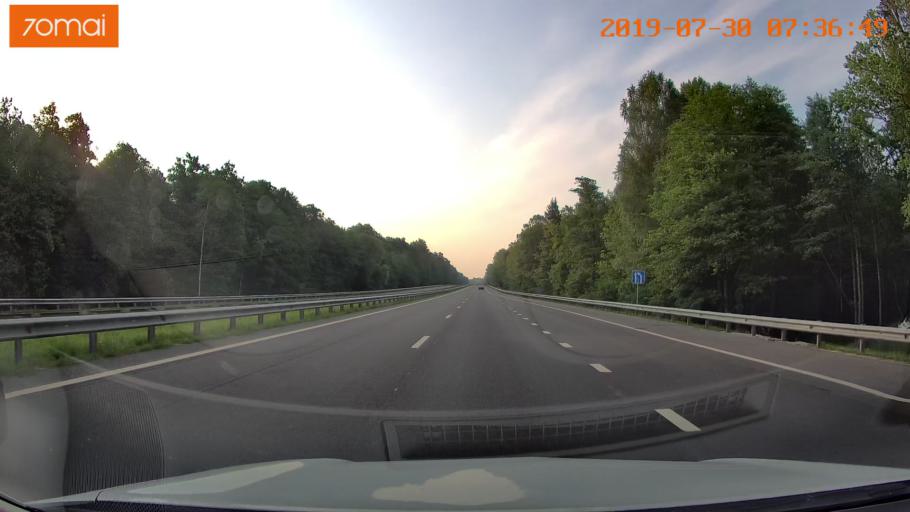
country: RU
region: Kaliningrad
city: Gvardeysk
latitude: 54.6612
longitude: 21.1326
